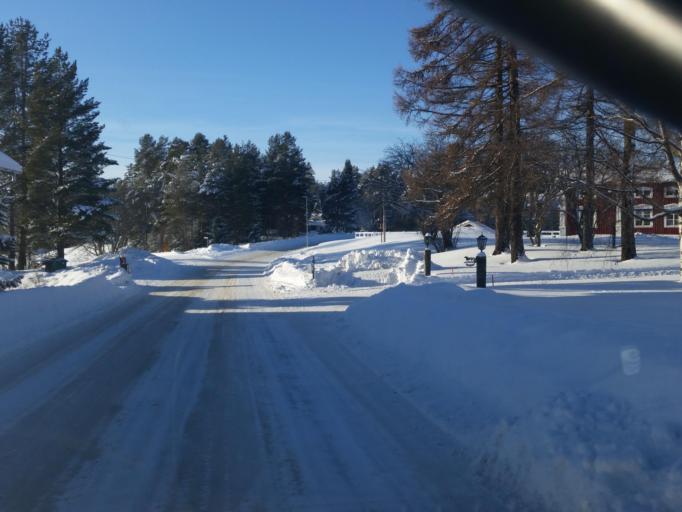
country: SE
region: Norrbotten
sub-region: Pitea Kommun
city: Bergsviken
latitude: 65.3069
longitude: 21.3699
